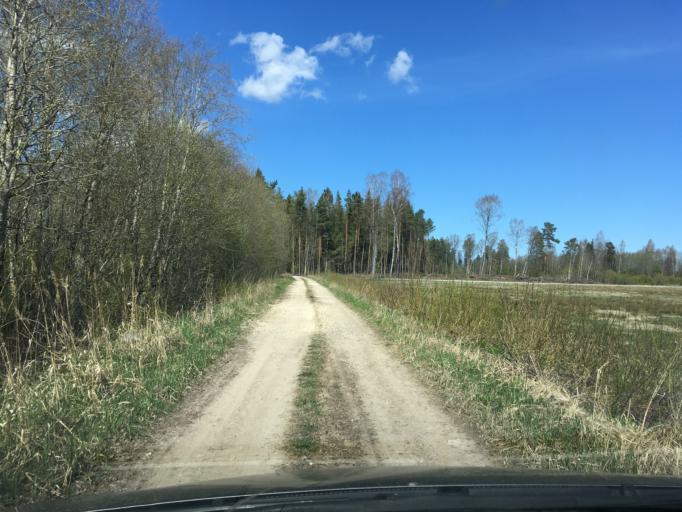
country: EE
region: Harju
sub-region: Raasiku vald
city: Arukula
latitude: 59.2088
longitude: 25.1185
